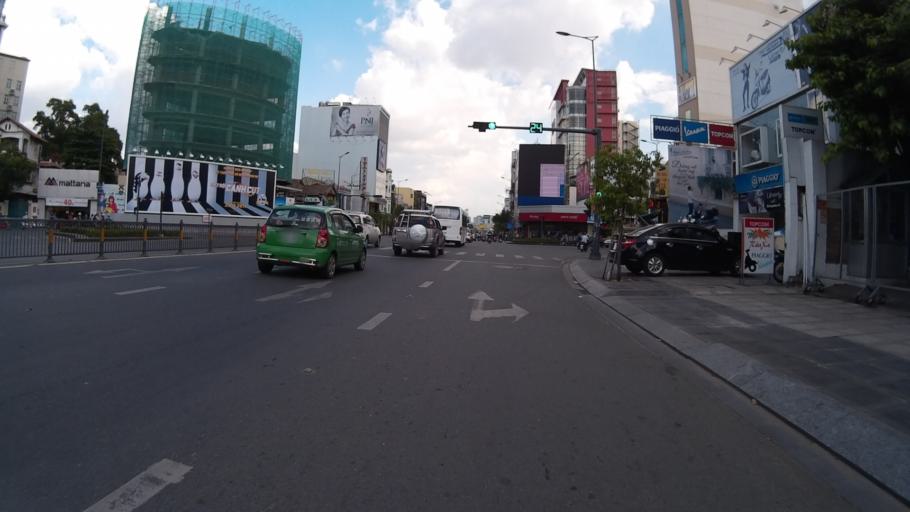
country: VN
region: Ho Chi Minh City
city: Quan Phu Nhuan
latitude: 10.7943
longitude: 106.6774
